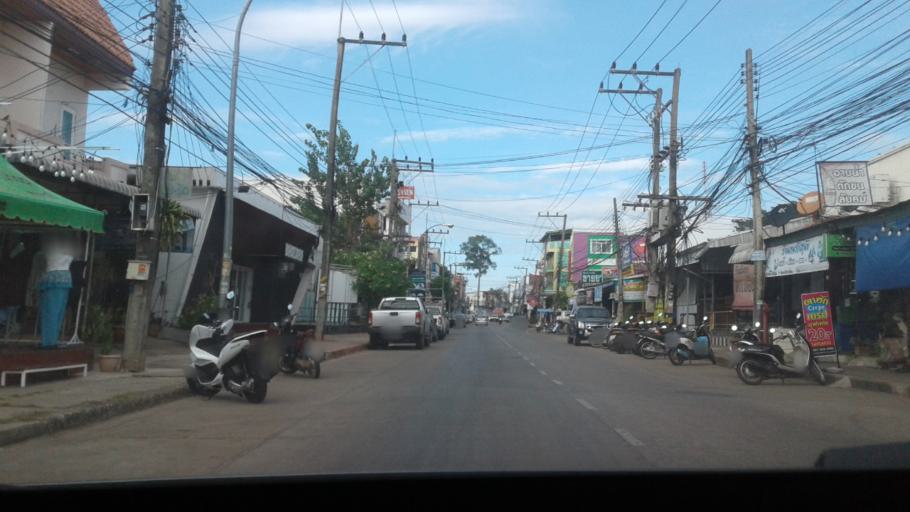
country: TH
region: Changwat Udon Thani
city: Udon Thani
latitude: 17.4138
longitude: 102.8001
